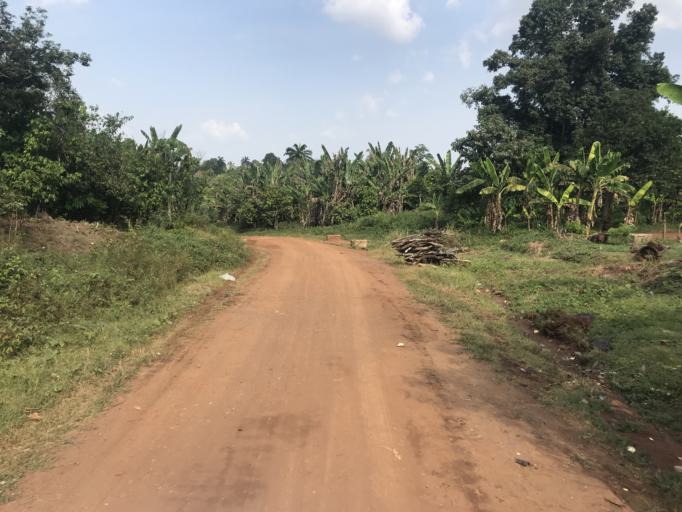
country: NG
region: Osun
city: Osu
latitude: 7.6479
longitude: 4.6618
